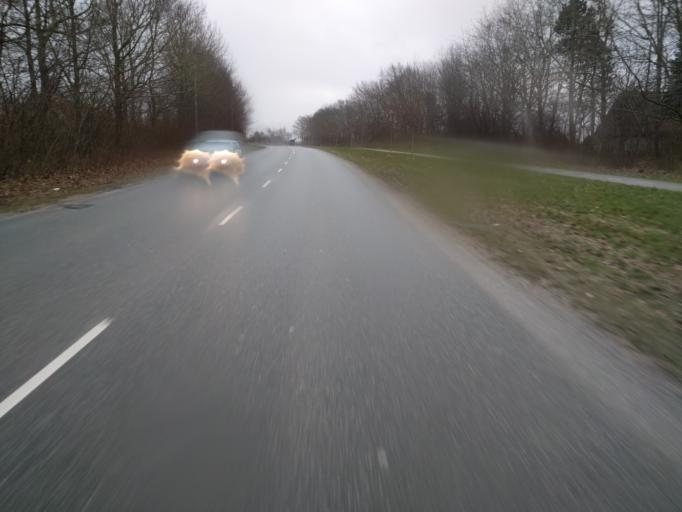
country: DK
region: Central Jutland
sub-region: Viborg Kommune
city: Viborg
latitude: 56.4553
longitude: 9.4454
